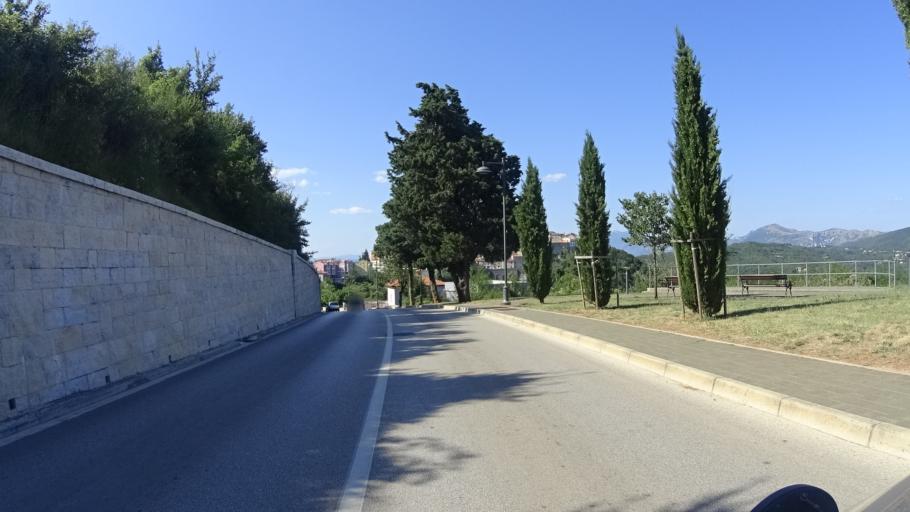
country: HR
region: Istarska
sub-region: Grad Labin
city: Labin
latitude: 45.0812
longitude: 14.1240
